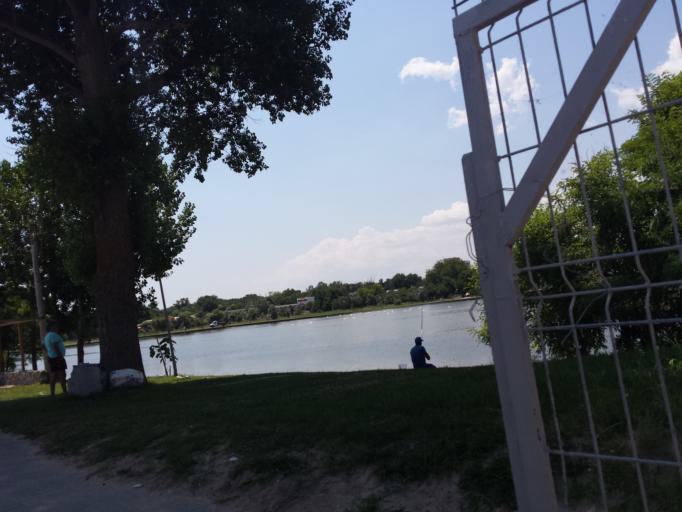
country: RO
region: Constanta
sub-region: Comuna Douazeci si Trei August
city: Douazeci si Trei August
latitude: 43.8621
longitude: 28.6058
